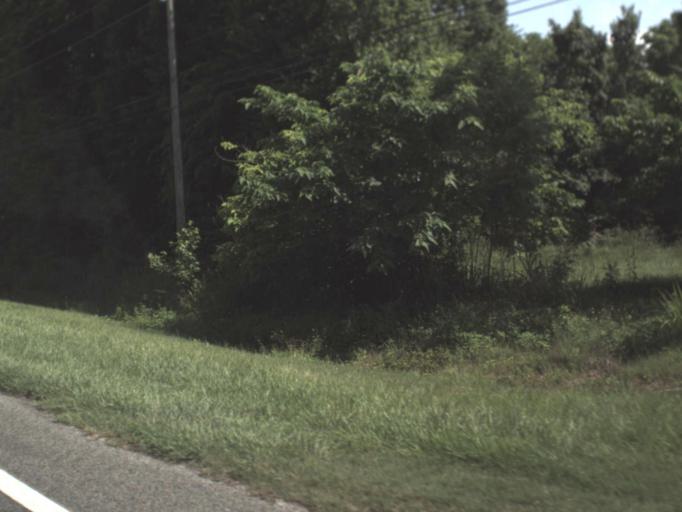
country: US
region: Florida
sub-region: Marion County
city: Citra
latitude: 29.4894
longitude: -82.2506
